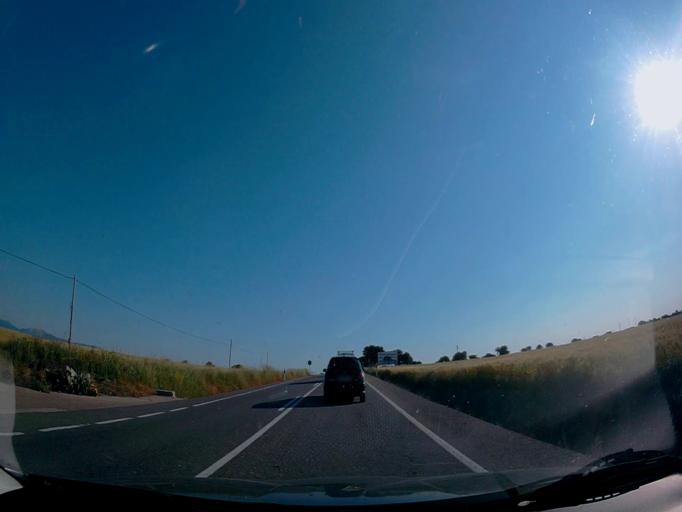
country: ES
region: Castille-La Mancha
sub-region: Province of Toledo
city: Escalona
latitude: 40.1272
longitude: -4.4060
